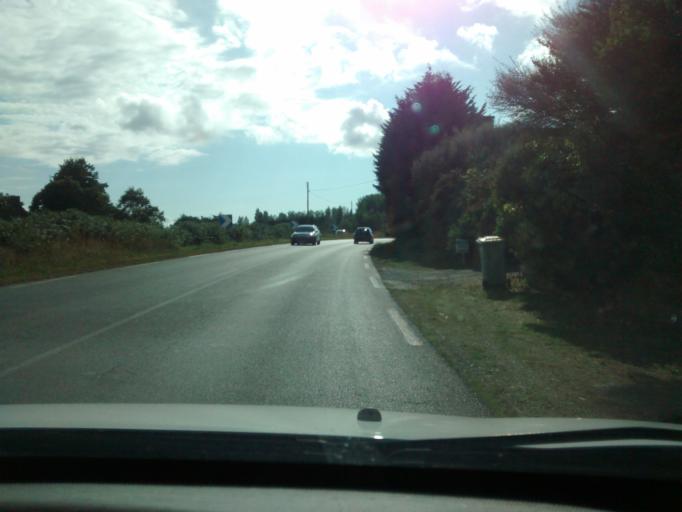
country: FR
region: Brittany
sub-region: Departement des Cotes-d'Armor
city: Rospez
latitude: 48.7410
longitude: -3.4219
